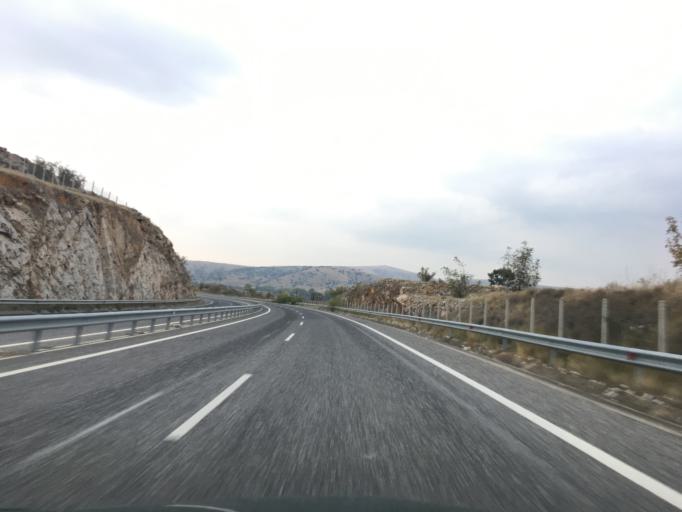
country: GR
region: Thessaly
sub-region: Trikala
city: Zarkos
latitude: 39.6039
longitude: 22.2089
